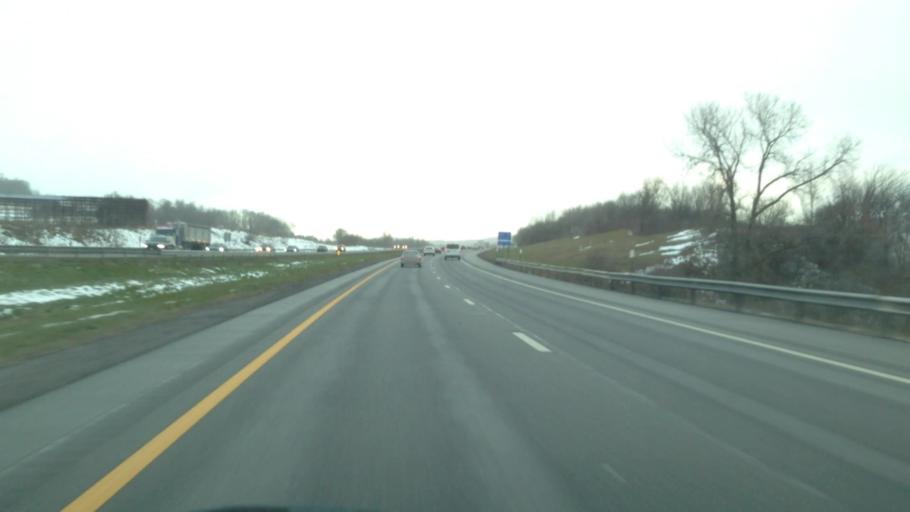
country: US
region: New York
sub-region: Montgomery County
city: Fort Plain
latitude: 42.9660
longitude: -74.6437
